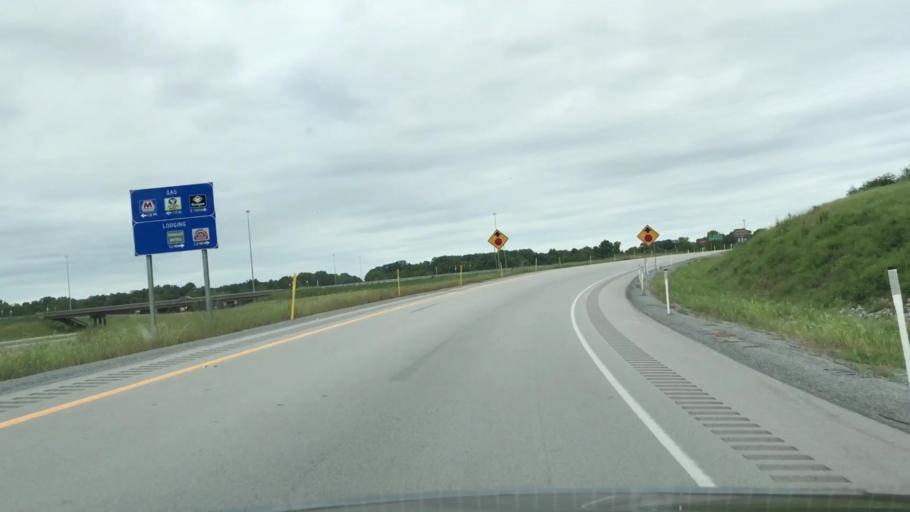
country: US
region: Kentucky
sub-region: Russell County
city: Russell Springs
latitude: 37.0530
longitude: -85.0672
